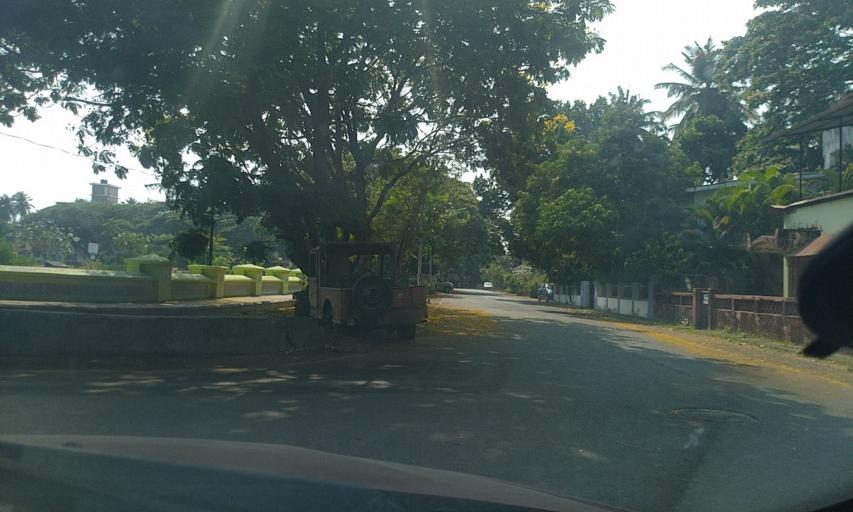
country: IN
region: Goa
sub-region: North Goa
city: Panaji
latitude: 15.4853
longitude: 73.8150
